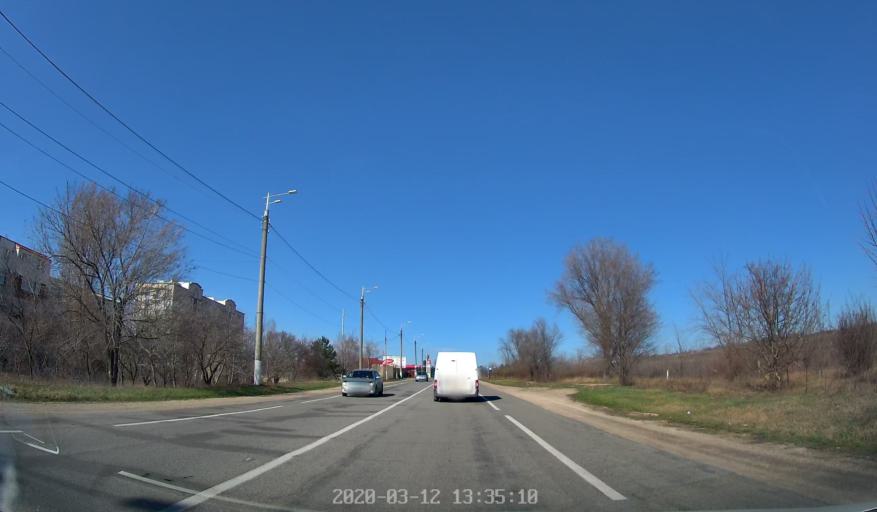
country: MD
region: Laloveni
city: Ialoveni
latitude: 46.9694
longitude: 28.7664
